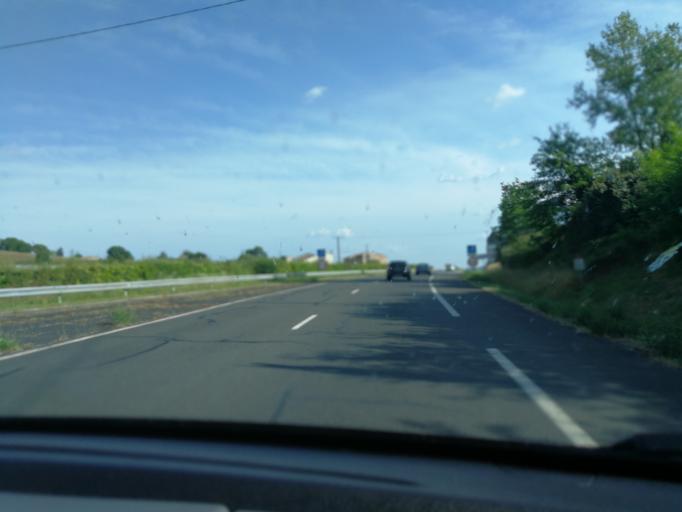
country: FR
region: Midi-Pyrenees
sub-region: Departement du Tarn
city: Arthes
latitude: 43.9694
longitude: 2.1832
